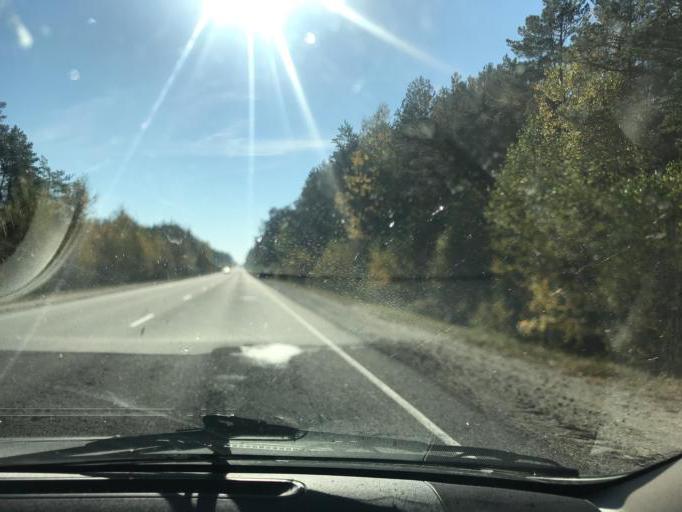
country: BY
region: Brest
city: Mikashevichy
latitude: 52.4380
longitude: 27.4707
